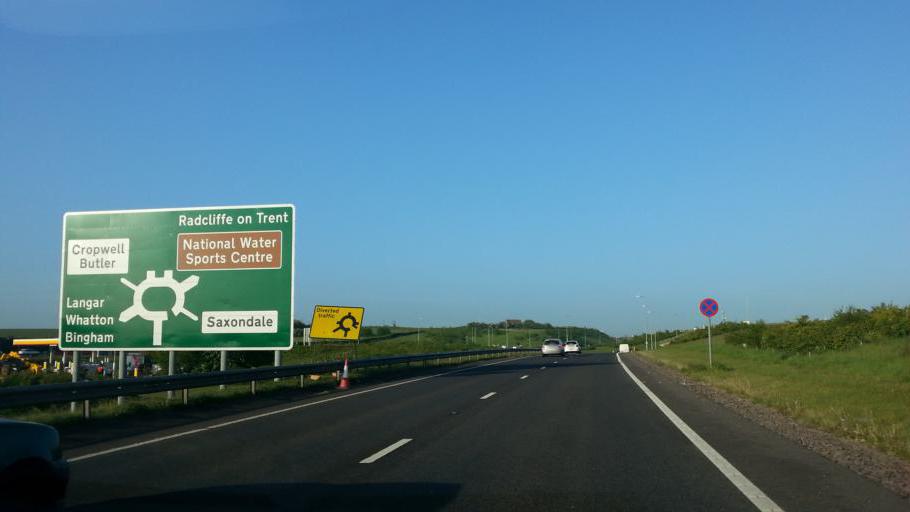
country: GB
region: England
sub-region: Nottinghamshire
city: Bingham
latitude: 52.9509
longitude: -0.9790
